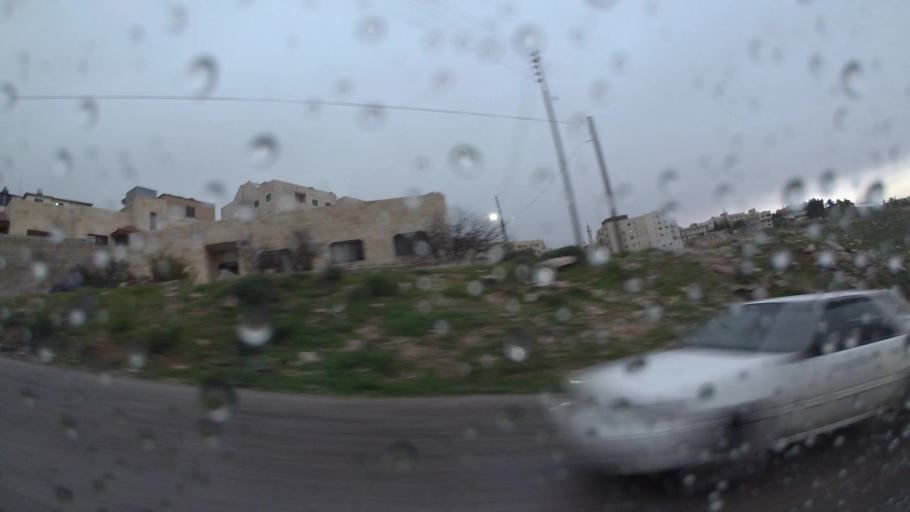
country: JO
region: Amman
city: Amman
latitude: 31.9987
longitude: 35.9687
